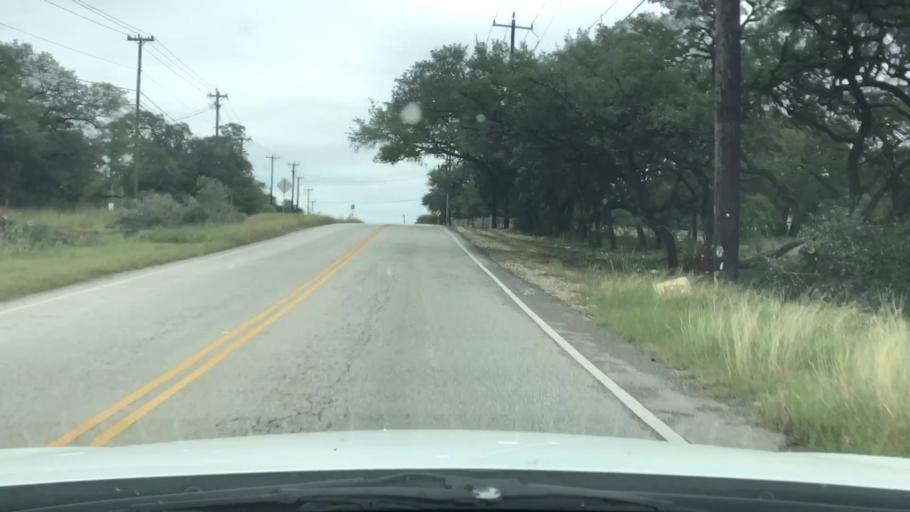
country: US
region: Texas
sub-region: Bexar County
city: Hollywood Park
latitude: 29.6463
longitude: -98.4061
